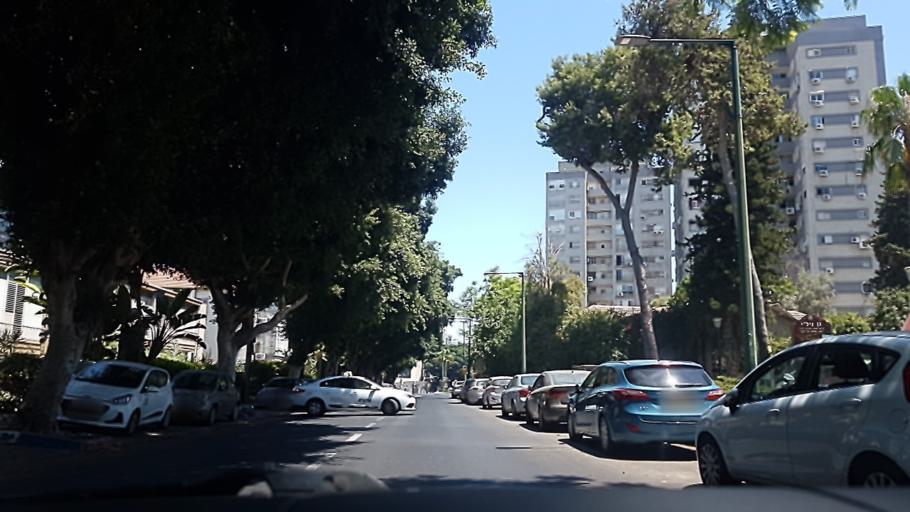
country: IL
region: Tel Aviv
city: Ramat Gan
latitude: 32.0865
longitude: 34.8089
